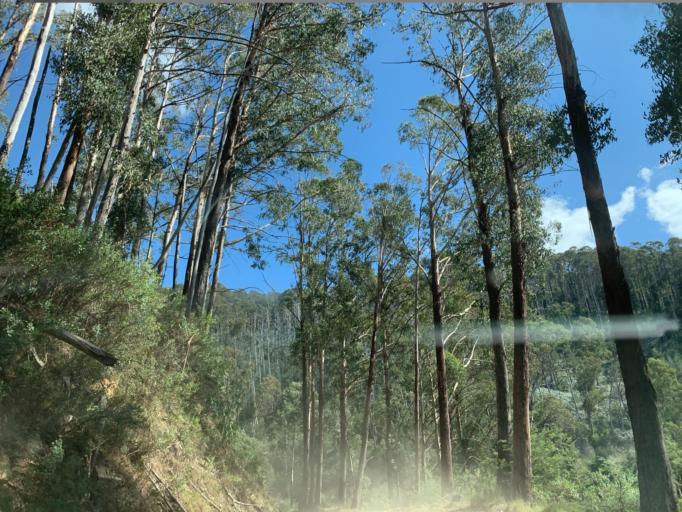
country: AU
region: Victoria
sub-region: Mansfield
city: Mansfield
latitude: -37.1007
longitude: 146.4831
